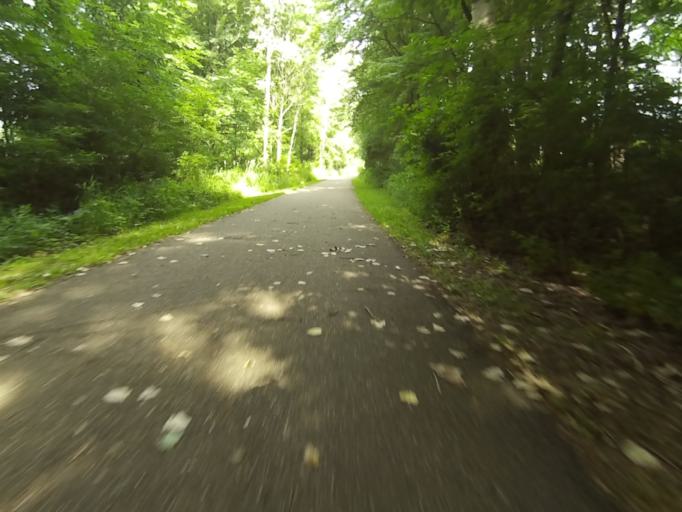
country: US
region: Ohio
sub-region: Portage County
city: Kent
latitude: 41.1884
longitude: -81.3878
